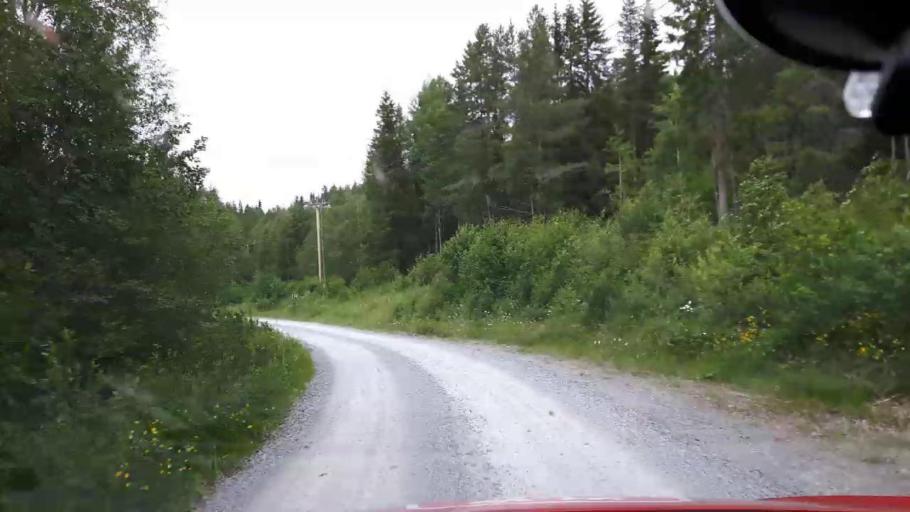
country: SE
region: Jaemtland
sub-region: OEstersunds Kommun
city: Brunflo
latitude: 63.0307
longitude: 14.9380
